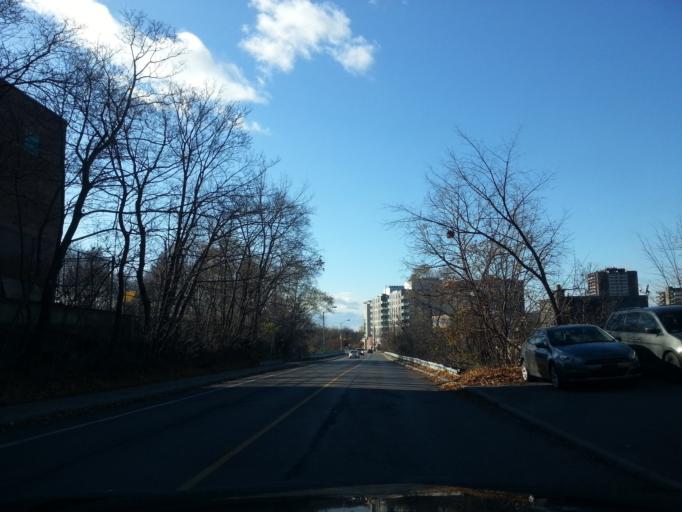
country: CA
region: Ontario
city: Ottawa
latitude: 45.3911
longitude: -75.7536
